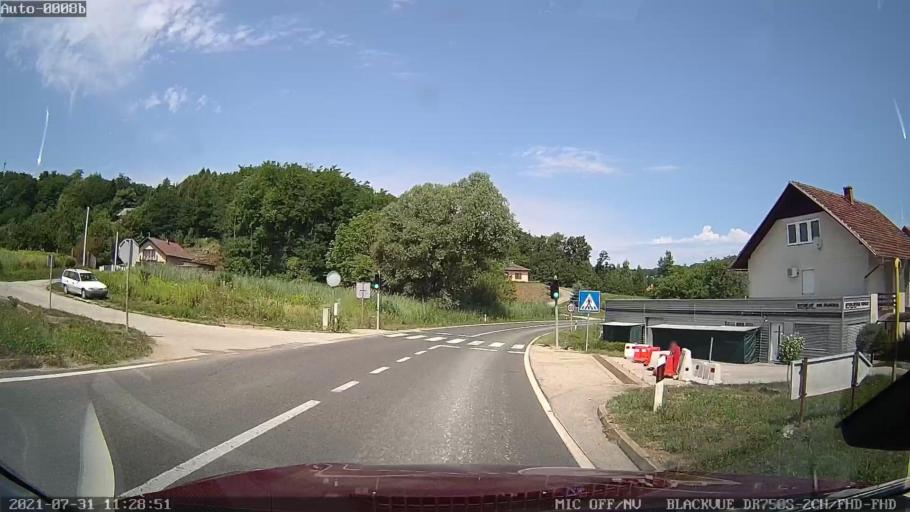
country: HR
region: Varazdinska
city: Ljubescica
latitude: 46.2030
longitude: 16.4210
